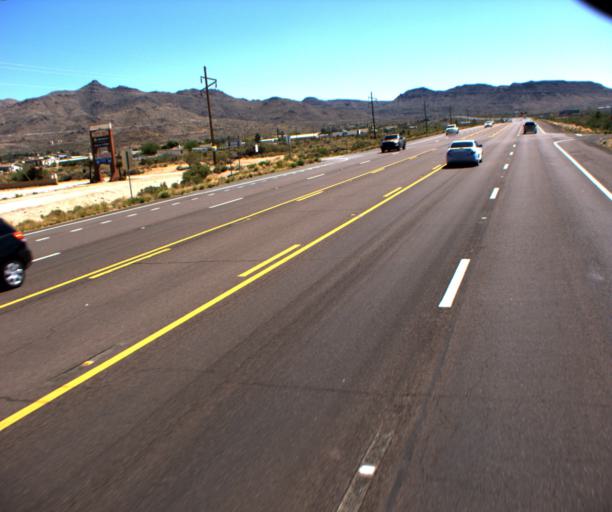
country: US
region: Arizona
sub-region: Mohave County
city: Golden Valley
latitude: 35.2189
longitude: -114.1529
